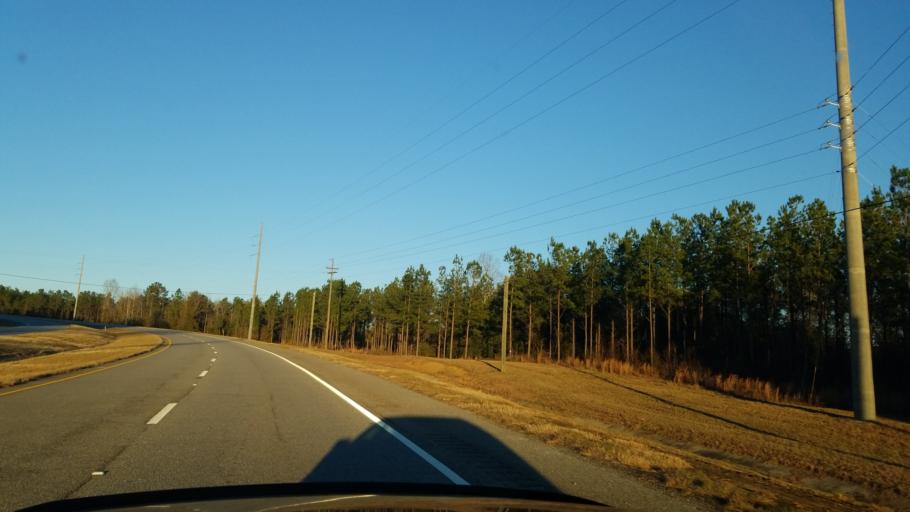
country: US
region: Georgia
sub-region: Chattahoochee County
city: Cusseta
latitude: 32.2726
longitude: -84.7830
